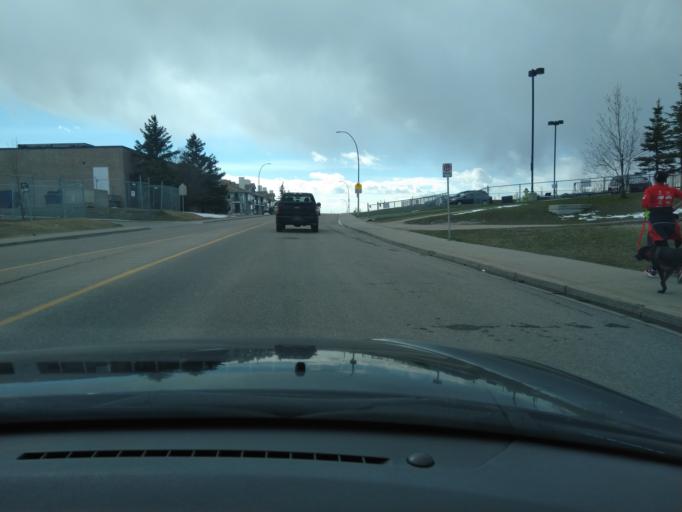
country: CA
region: Alberta
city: Calgary
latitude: 51.1341
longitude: -114.2093
